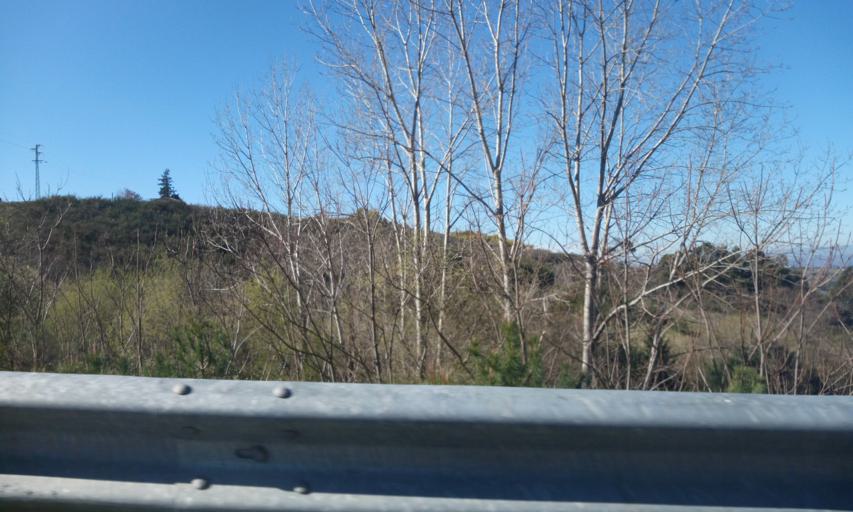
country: PT
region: Guarda
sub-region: Manteigas
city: Manteigas
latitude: 40.5125
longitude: -7.5644
